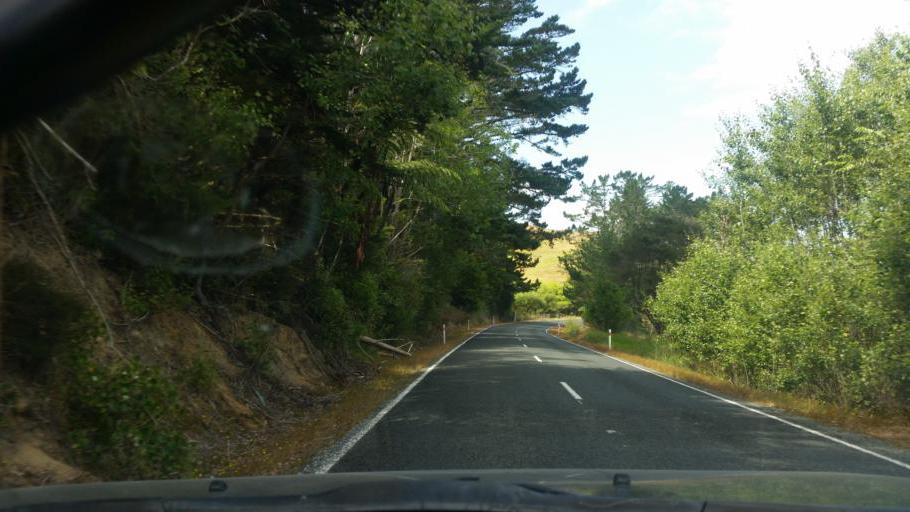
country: NZ
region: Northland
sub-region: Whangarei
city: Ruakaka
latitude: -35.9478
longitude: 174.2934
